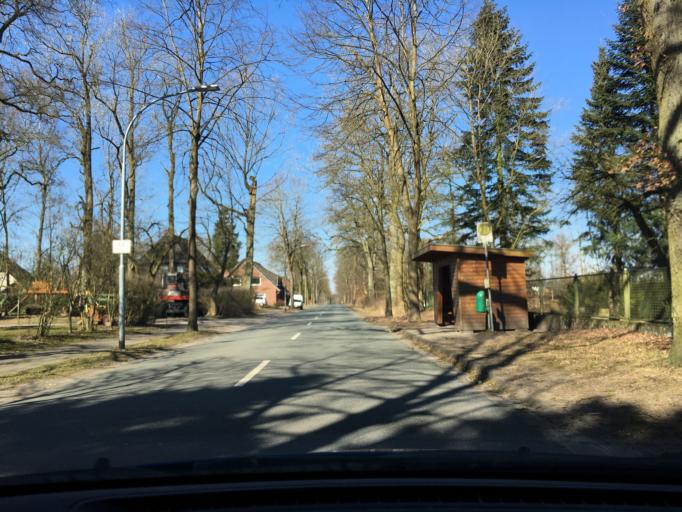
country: DE
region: Lower Saxony
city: Schneverdingen
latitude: 53.0841
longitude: 9.7657
